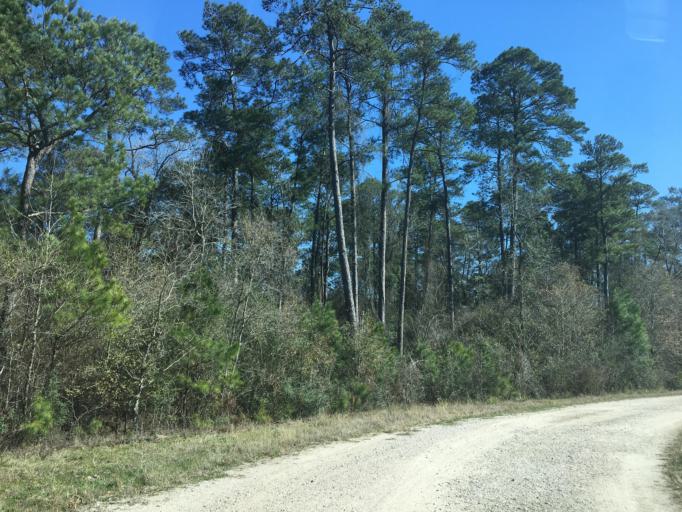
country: US
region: Texas
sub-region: Harris County
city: Spring
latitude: 30.1018
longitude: -95.4556
